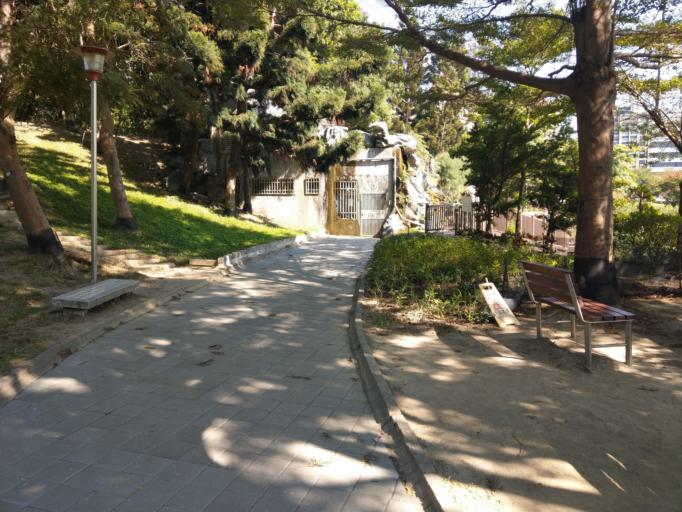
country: TW
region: Taiwan
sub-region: Taichung City
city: Taichung
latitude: 24.1313
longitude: 120.6420
